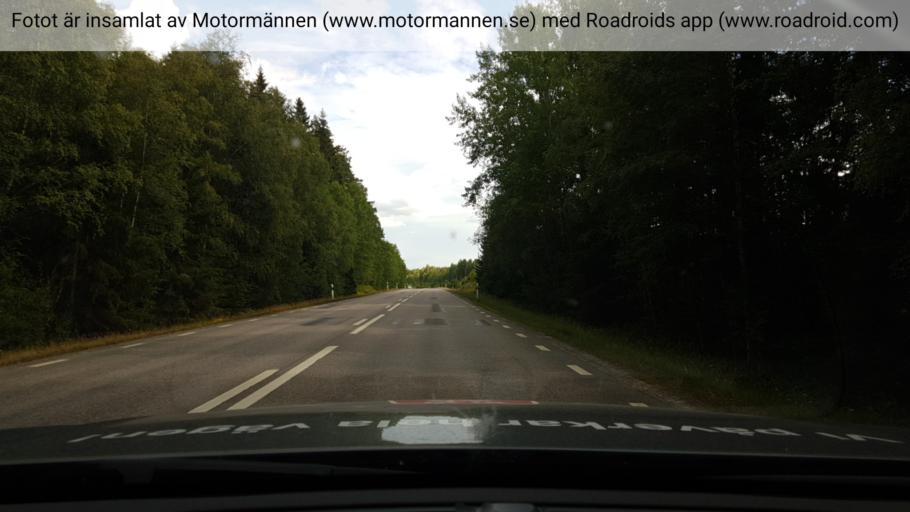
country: SE
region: Uppsala
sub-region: Heby Kommun
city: Morgongava
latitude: 59.9009
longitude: 17.0841
